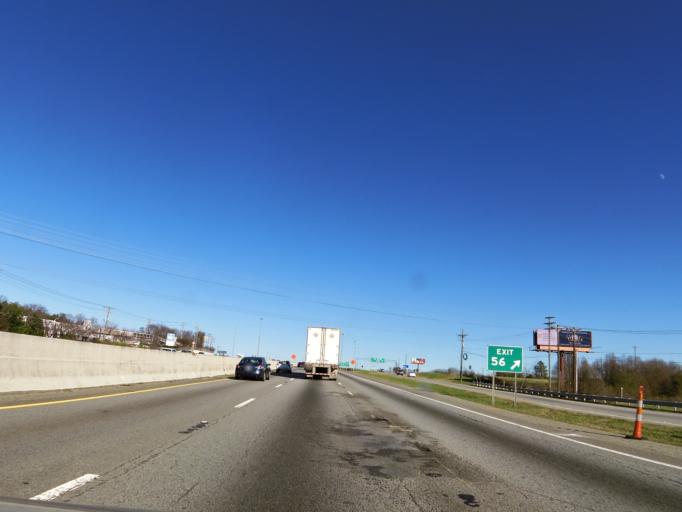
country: US
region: South Carolina
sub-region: Greenville County
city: Five Forks
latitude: 34.8697
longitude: -82.2298
